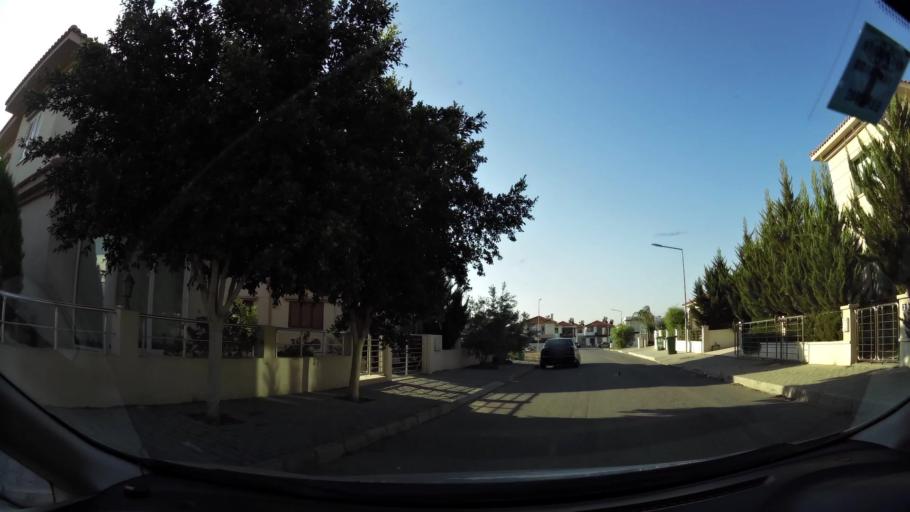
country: CY
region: Lefkosia
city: Nicosia
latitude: 35.2034
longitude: 33.3045
